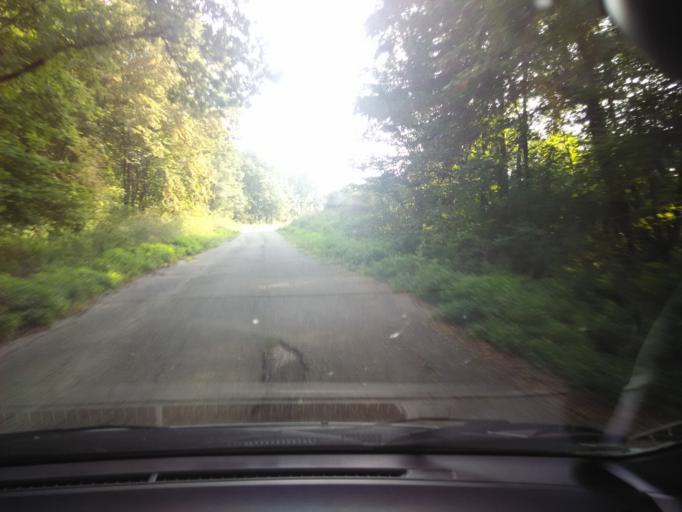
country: SK
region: Nitriansky
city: Levice
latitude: 48.2925
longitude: 18.7014
